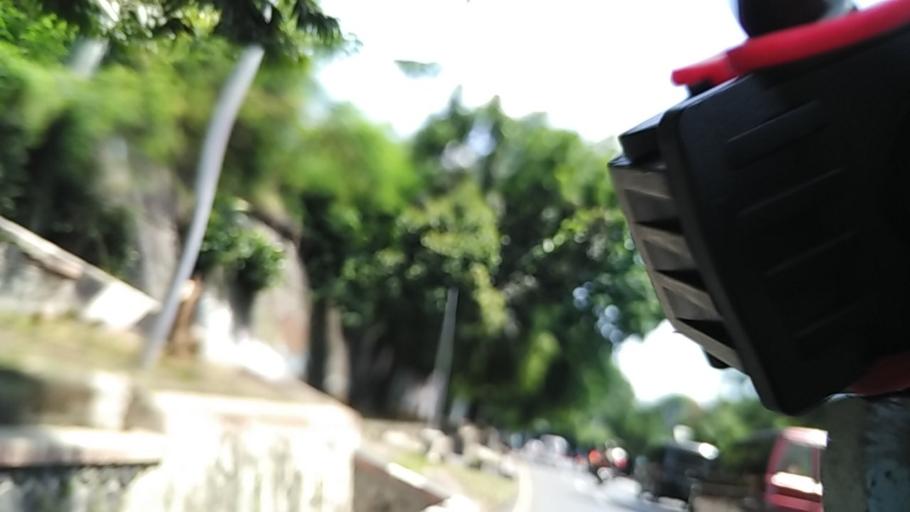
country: ID
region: Central Java
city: Semarang
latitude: -6.9970
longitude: 110.4069
